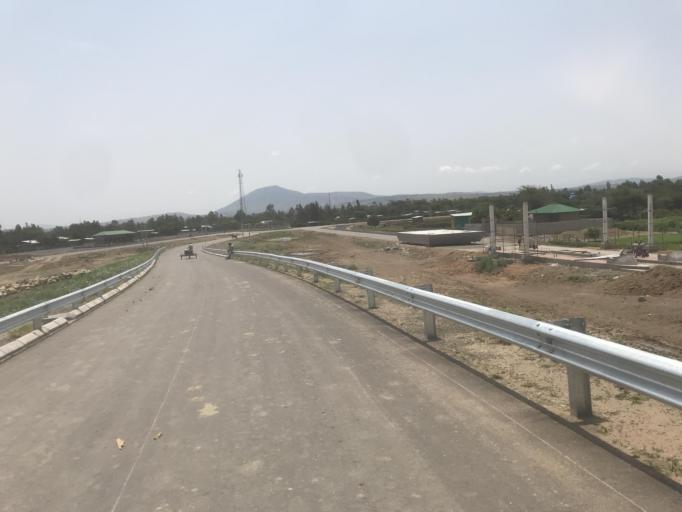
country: ET
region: Oromiya
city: Mojo
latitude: 8.3012
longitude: 38.9377
